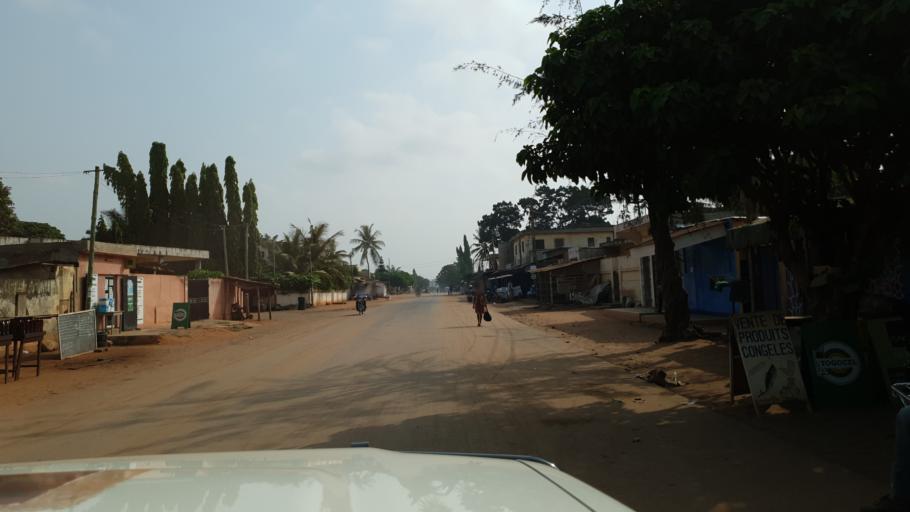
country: TG
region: Maritime
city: Lome
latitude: 6.1545
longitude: 1.2174
